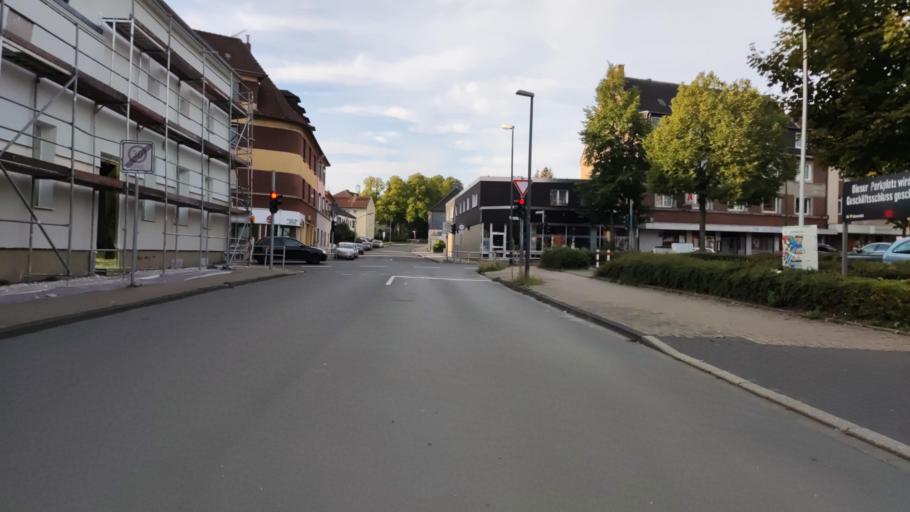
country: DE
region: North Rhine-Westphalia
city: Castrop-Rauxel
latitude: 51.5491
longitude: 7.2803
